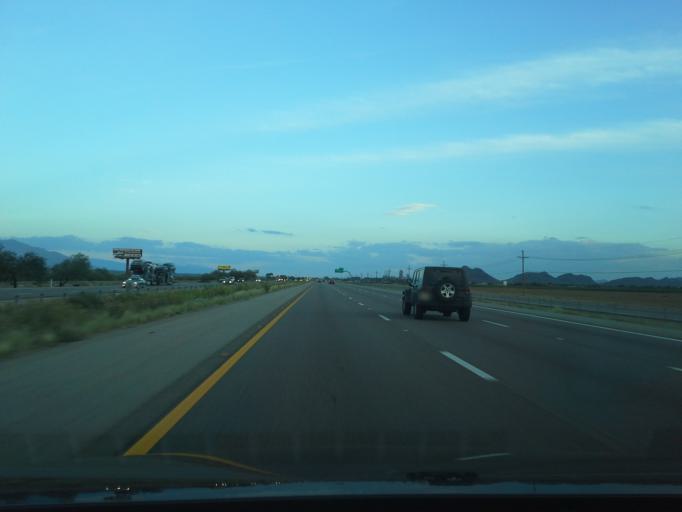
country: US
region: Arizona
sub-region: Pima County
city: Marana
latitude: 32.4348
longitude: -111.1782
